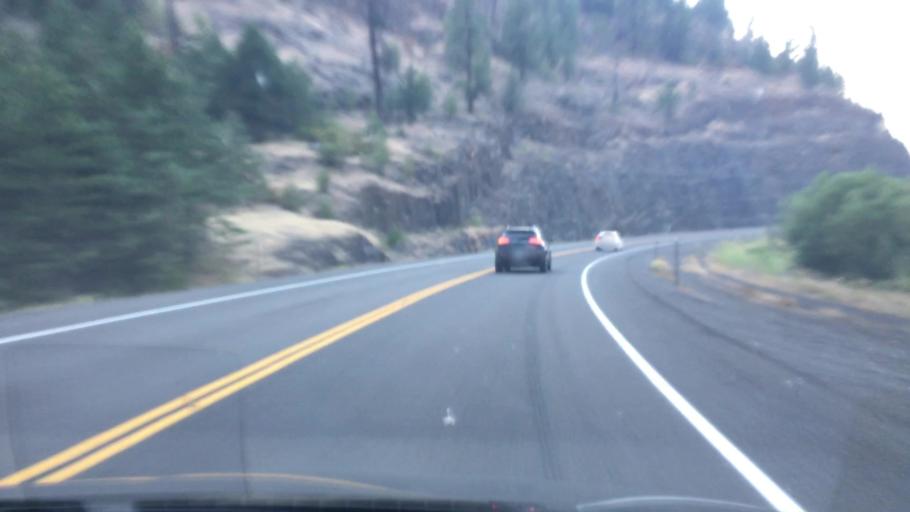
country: US
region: Idaho
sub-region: Valley County
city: McCall
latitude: 45.1943
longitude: -116.3083
